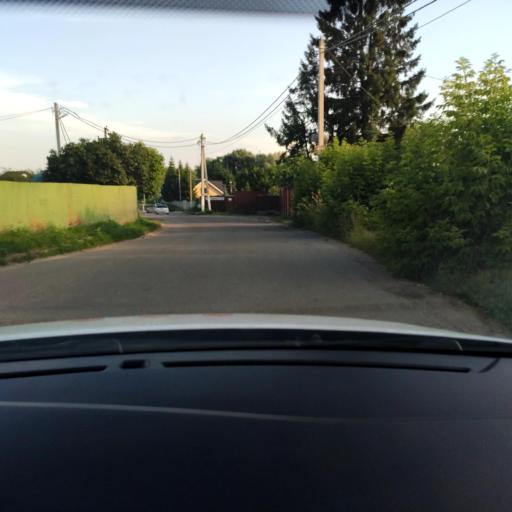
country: RU
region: Tatarstan
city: Vysokaya Gora
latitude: 55.9756
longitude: 49.3062
